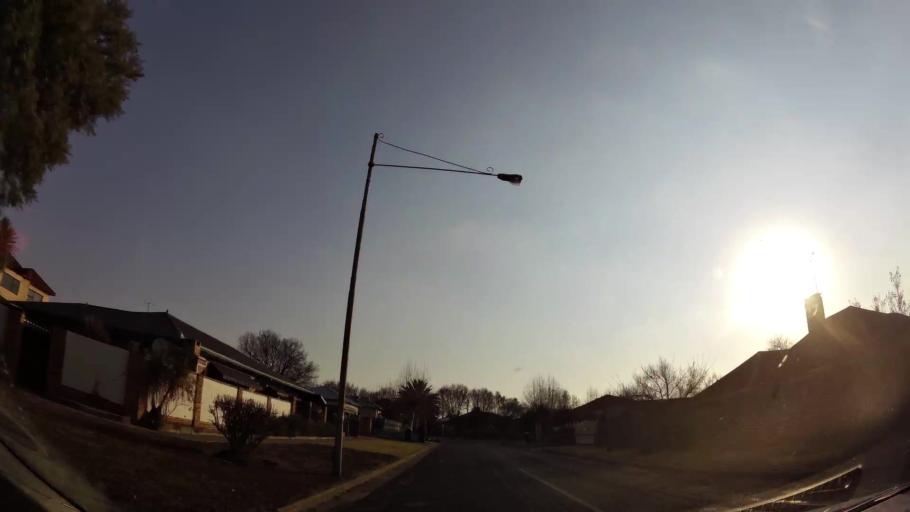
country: ZA
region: Gauteng
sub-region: Ekurhuleni Metropolitan Municipality
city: Springs
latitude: -26.2917
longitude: 28.4452
